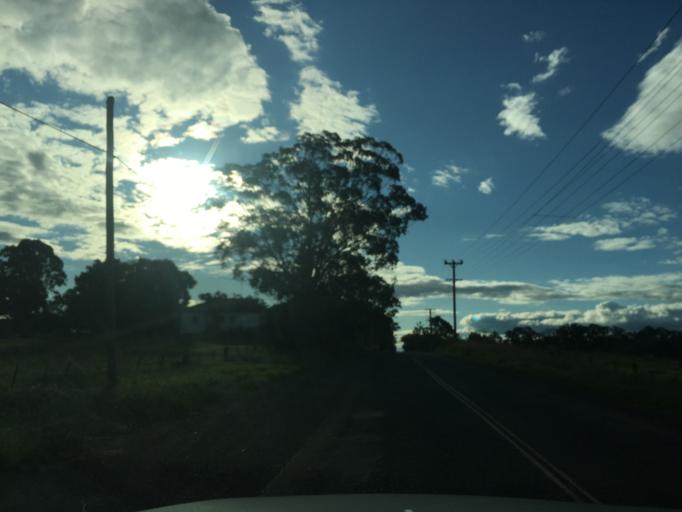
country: AU
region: New South Wales
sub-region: Campbelltown Municipality
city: Denham Court
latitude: -33.9698
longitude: 150.8007
